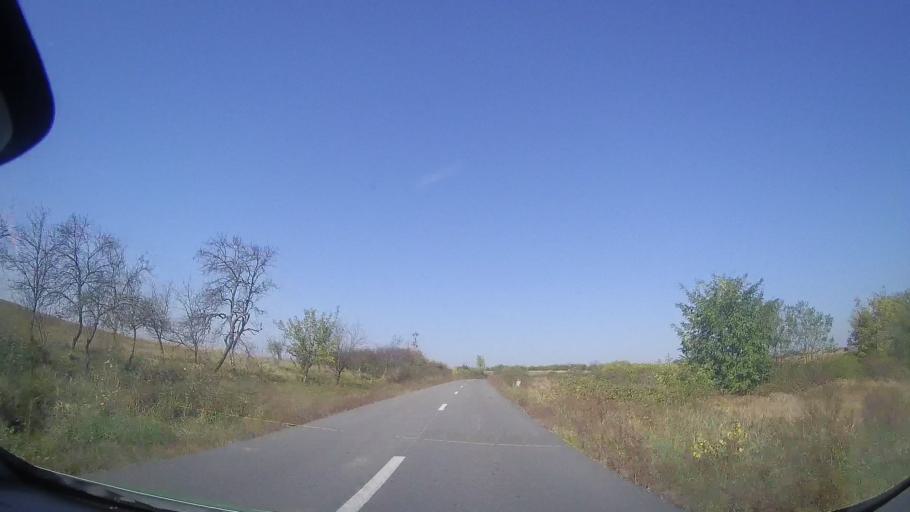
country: RO
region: Timis
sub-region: Comuna Balint
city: Balint
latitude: 45.8219
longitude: 21.8511
